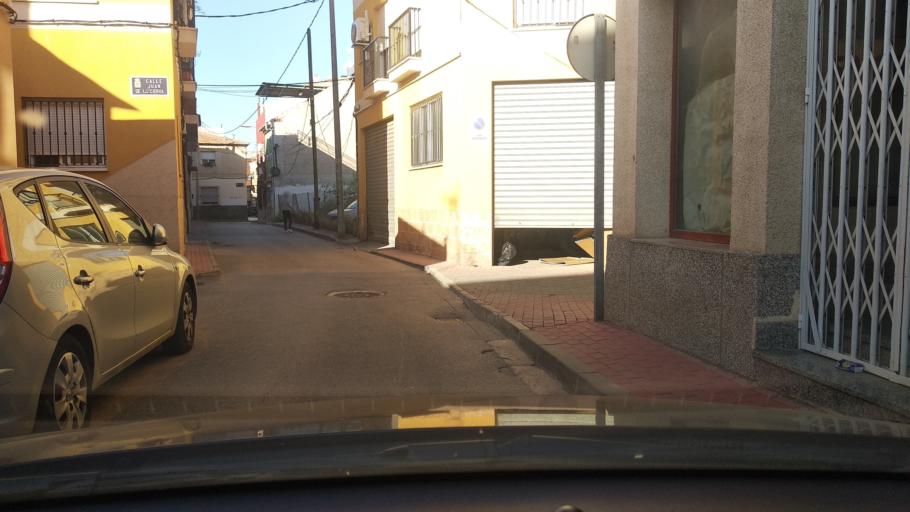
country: ES
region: Murcia
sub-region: Murcia
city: Murcia
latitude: 37.9434
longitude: -1.1291
